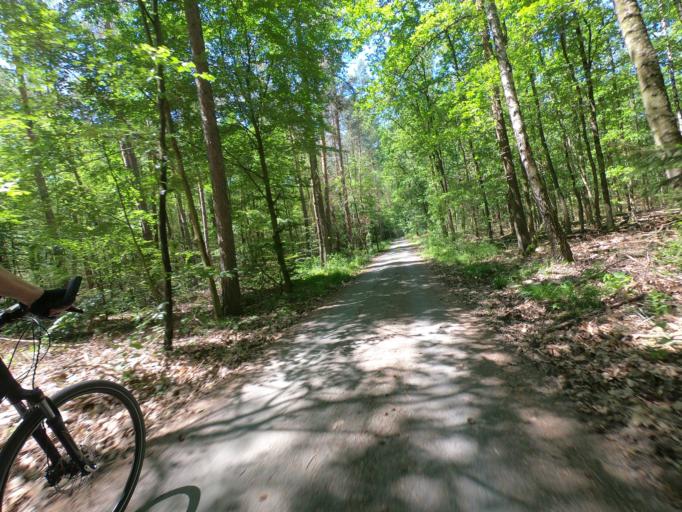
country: DE
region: Hesse
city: Niederrad
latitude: 50.0418
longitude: 8.6398
